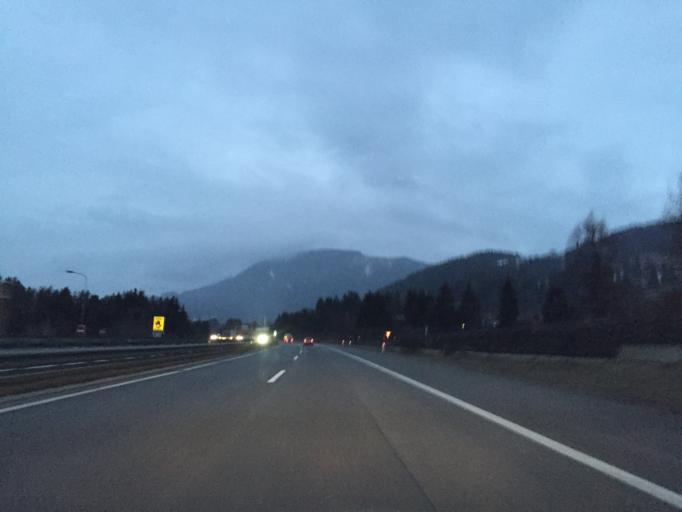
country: AT
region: Salzburg
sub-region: Politischer Bezirk Sankt Johann im Pongau
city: Eben im Pongau
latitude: 47.4216
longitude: 13.3808
